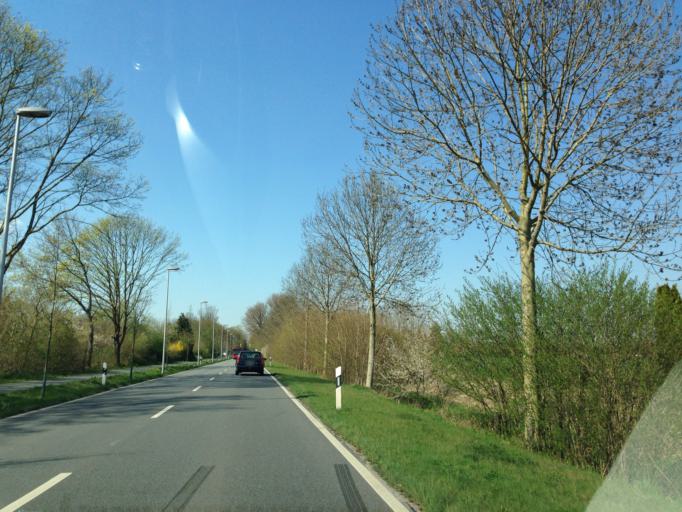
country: DE
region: North Rhine-Westphalia
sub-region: Regierungsbezirk Munster
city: Muenster
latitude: 51.9906
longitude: 7.6241
